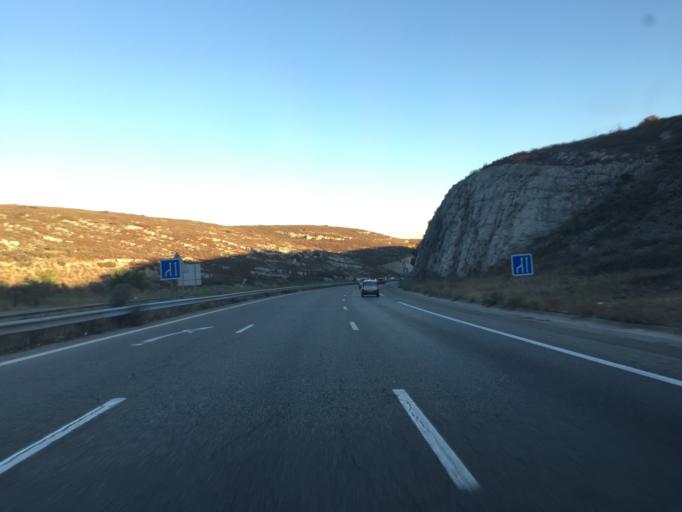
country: FR
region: Provence-Alpes-Cote d'Azur
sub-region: Departement des Bouches-du-Rhone
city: Les Pennes-Mirabeau
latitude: 43.3856
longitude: 5.3103
